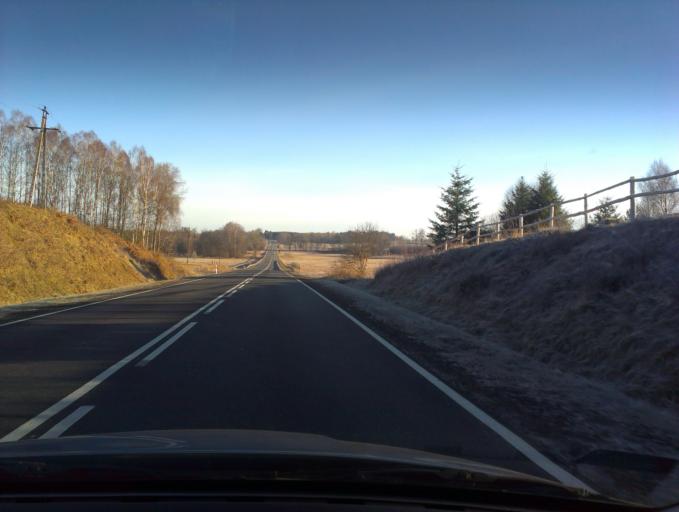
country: PL
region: West Pomeranian Voivodeship
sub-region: Powiat koszalinski
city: Bobolice
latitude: 53.8917
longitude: 16.6130
